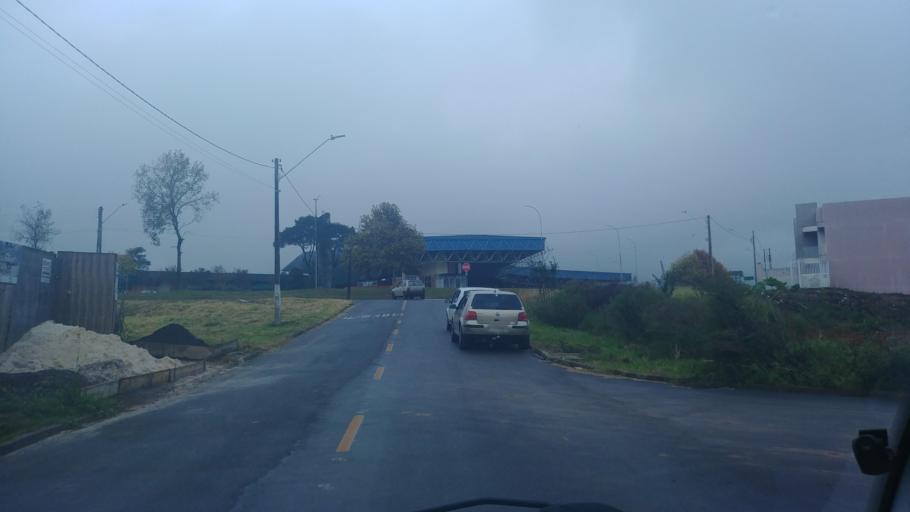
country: BR
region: Parana
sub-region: Guarapuava
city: Guarapuava
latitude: -25.3795
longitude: -51.4792
